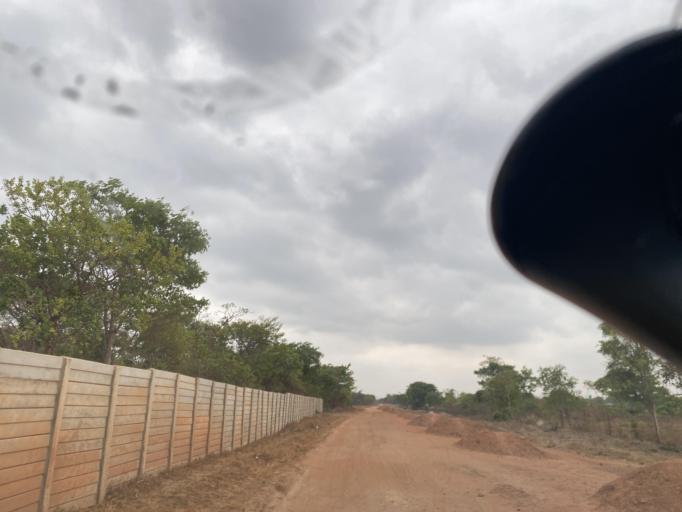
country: ZM
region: Lusaka
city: Chongwe
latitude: -15.2780
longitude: 28.7301
